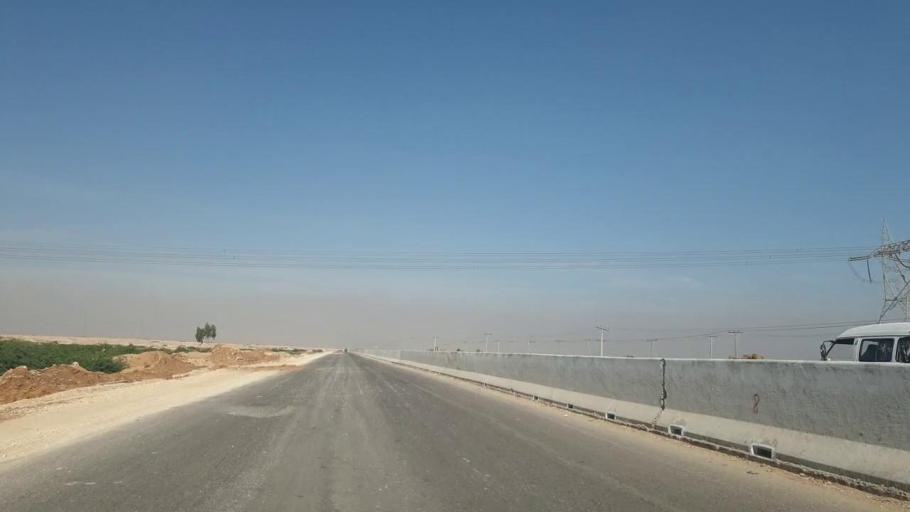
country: PK
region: Sindh
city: Jamshoro
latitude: 25.4842
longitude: 68.2720
